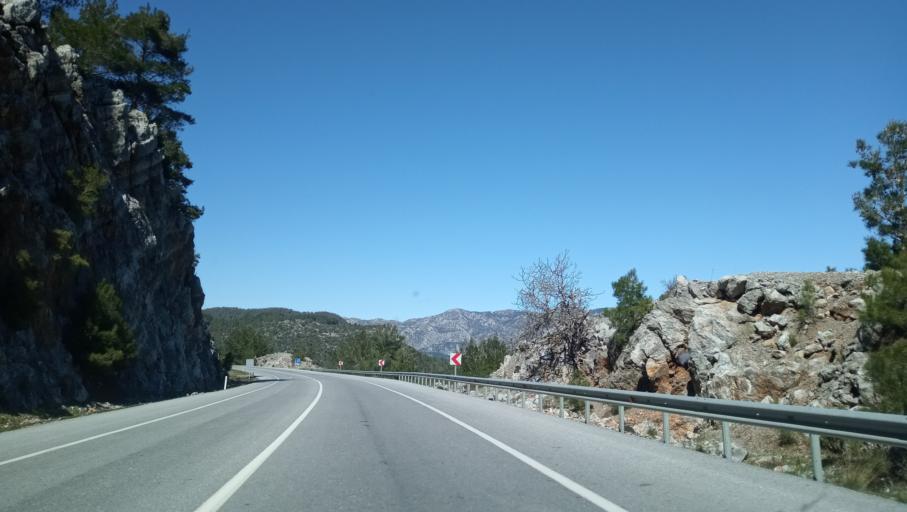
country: TR
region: Antalya
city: Guzelsu
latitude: 36.8409
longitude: 31.7913
